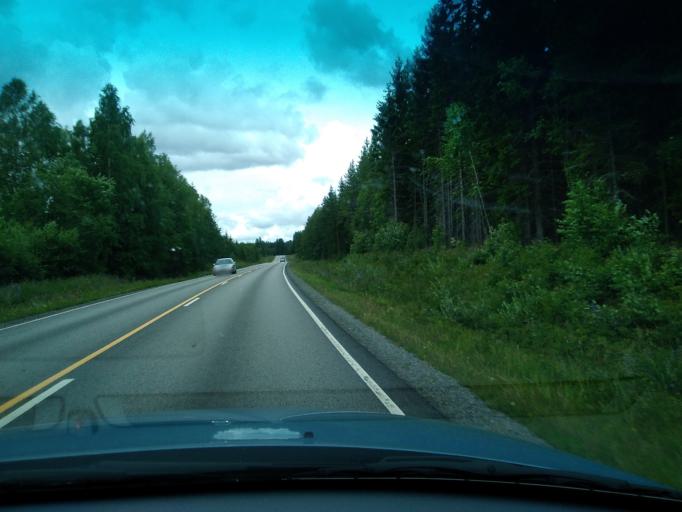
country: FI
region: Central Finland
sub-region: Saarijaervi-Viitasaari
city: Pylkoenmaeki
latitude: 62.6491
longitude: 25.0030
